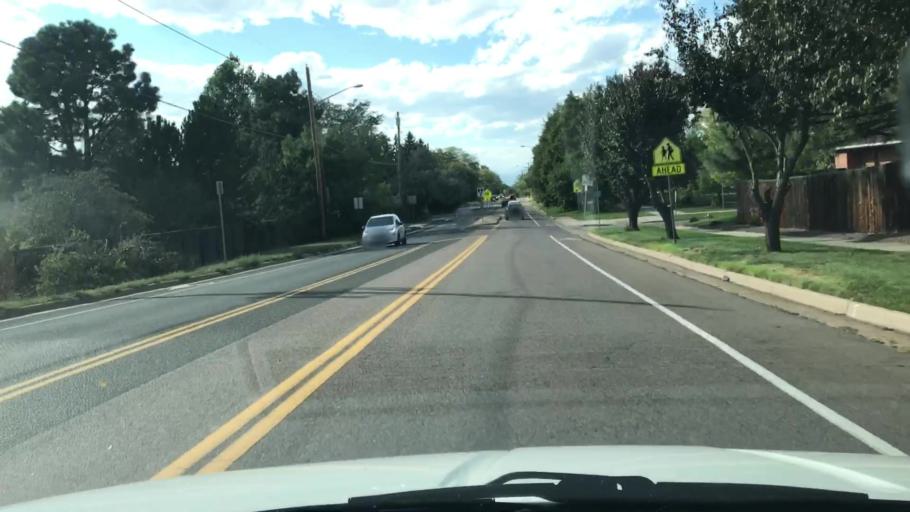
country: US
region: Colorado
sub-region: Arapahoe County
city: Cherry Hills Village
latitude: 39.6440
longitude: -104.9201
